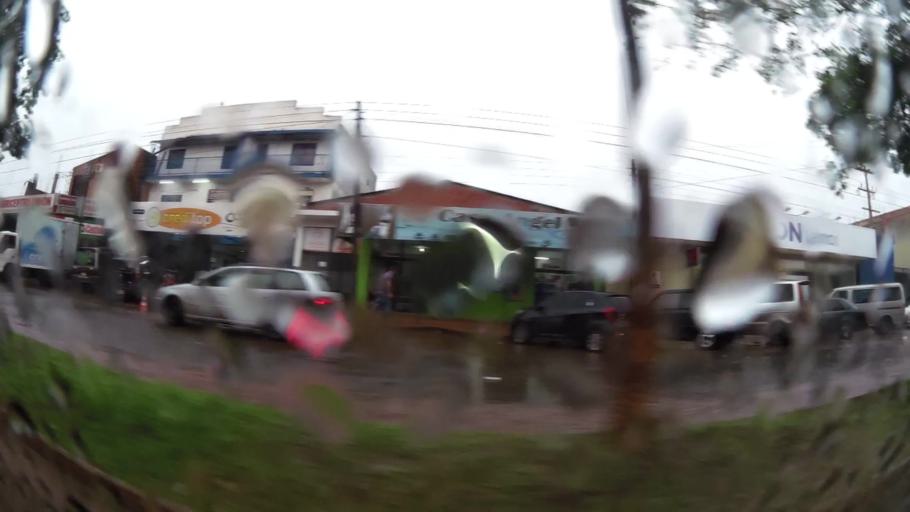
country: PY
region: Alto Parana
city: Ciudad del Este
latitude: -25.5014
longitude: -54.6676
